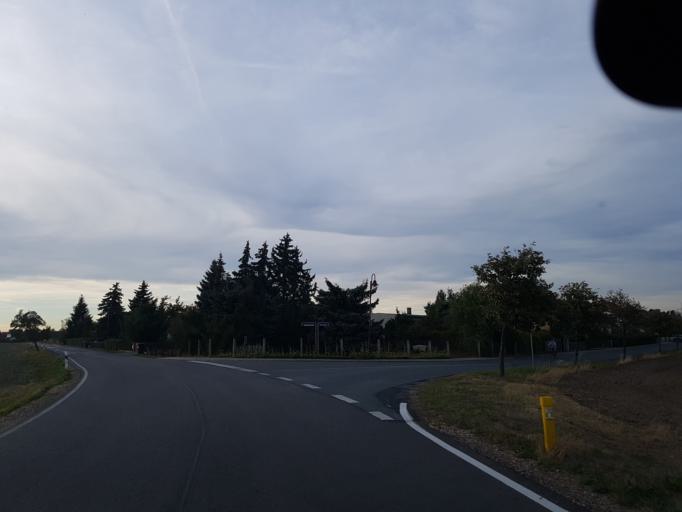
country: DE
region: Saxony
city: Wulknitz
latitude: 51.3661
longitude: 13.4011
